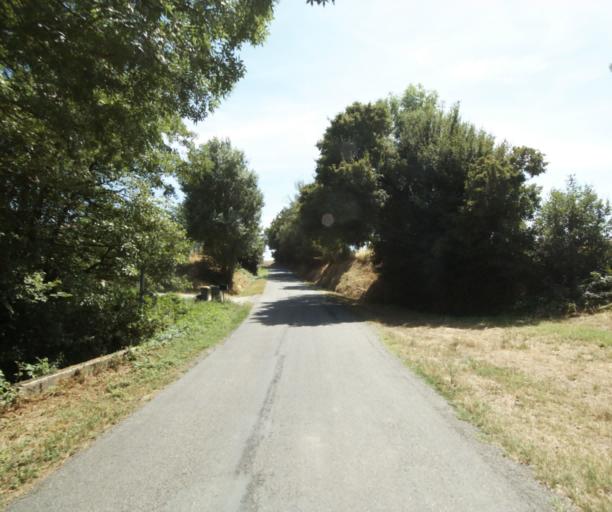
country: FR
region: Midi-Pyrenees
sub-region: Departement de la Haute-Garonne
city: Revel
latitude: 43.4948
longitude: 2.0214
